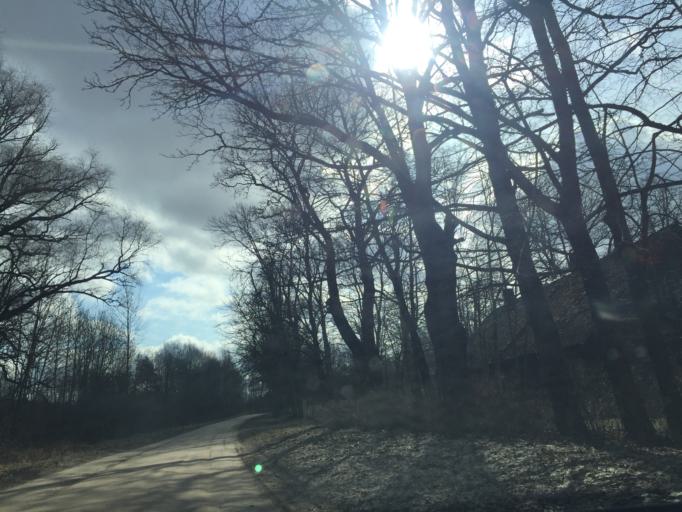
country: LV
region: Vecumnieki
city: Vecumnieki
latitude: 56.5899
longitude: 24.5580
